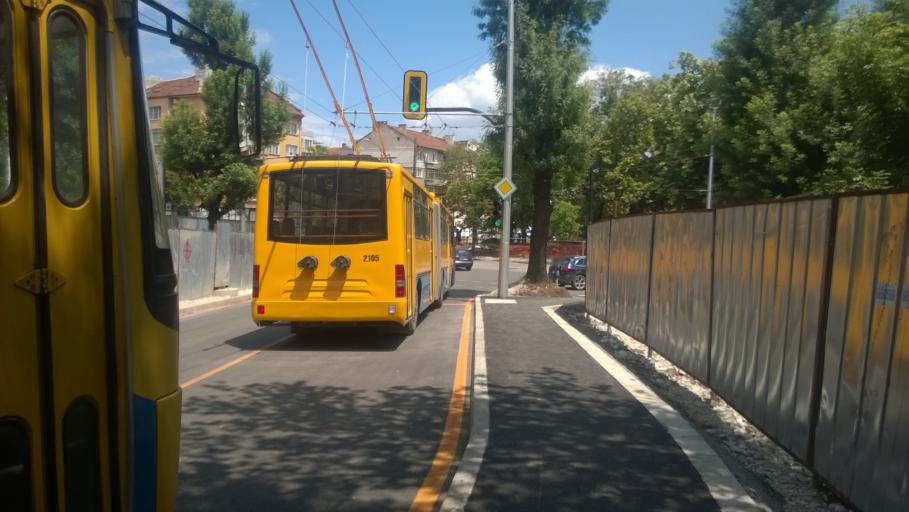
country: BG
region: Sofia-Capital
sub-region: Stolichna Obshtina
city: Sofia
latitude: 42.6863
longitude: 23.3106
